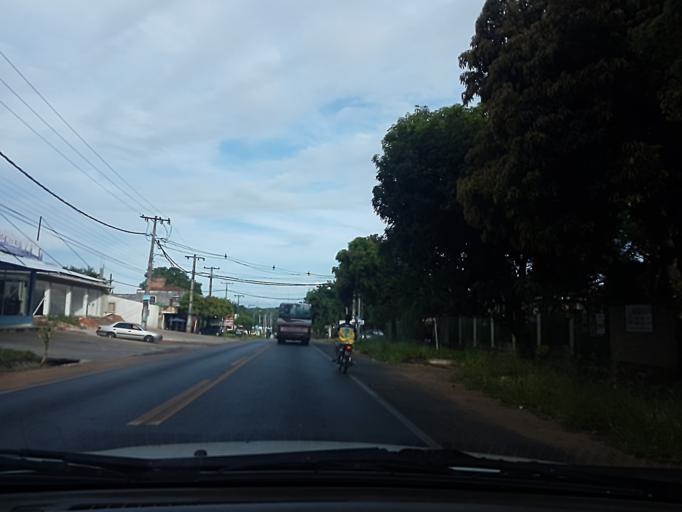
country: PY
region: Central
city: San Lorenzo
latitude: -25.2826
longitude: -57.4693
